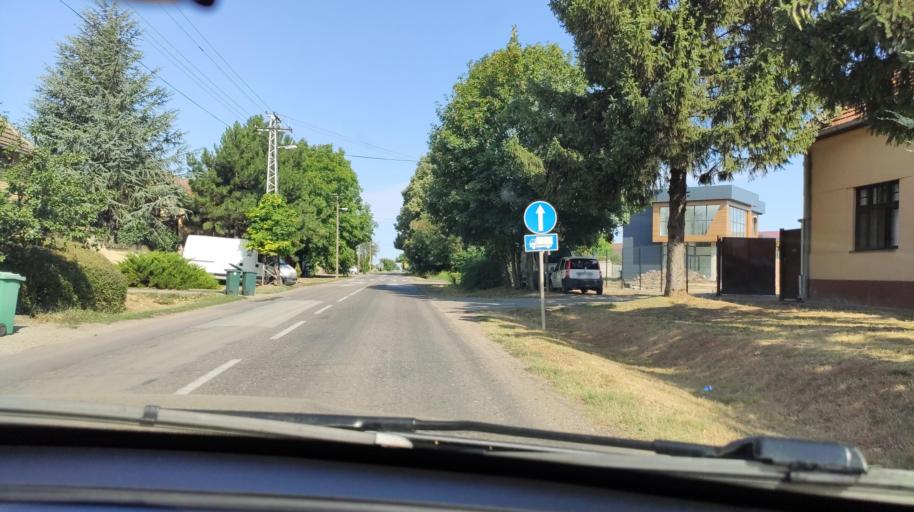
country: RS
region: Autonomna Pokrajina Vojvodina
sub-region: Severnobacki Okrug
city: Backa Topola
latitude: 45.8147
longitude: 19.6181
